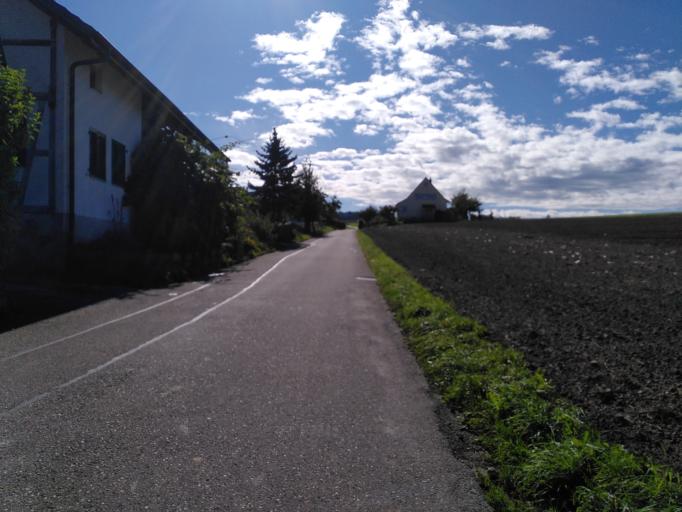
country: CH
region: Bern
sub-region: Oberaargau
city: Seeberg
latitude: 47.1399
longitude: 7.7132
